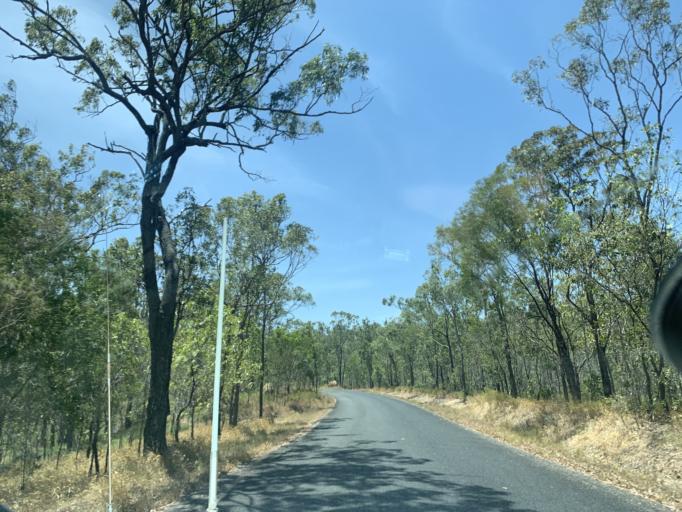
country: AU
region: Queensland
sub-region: Tablelands
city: Kuranda
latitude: -16.9180
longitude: 145.5822
